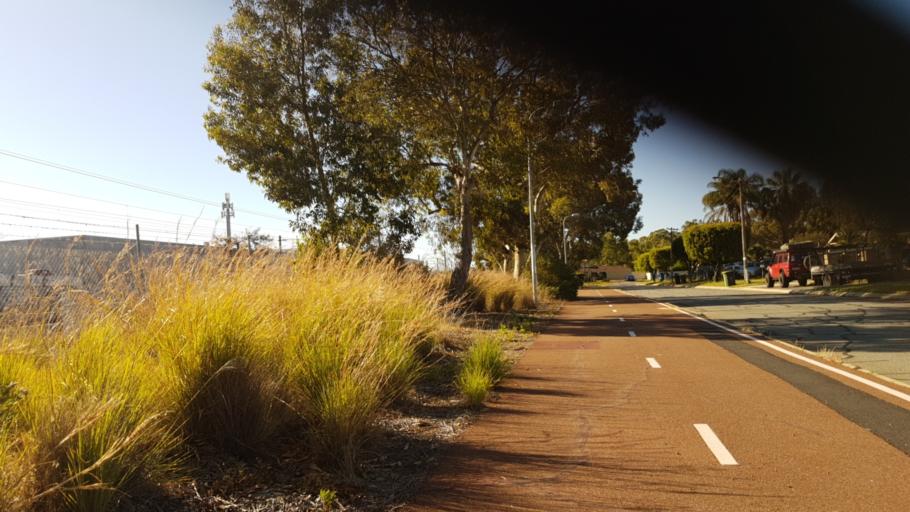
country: AU
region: Western Australia
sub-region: Gosnells
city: Kenwick
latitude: -32.0400
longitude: 115.9734
